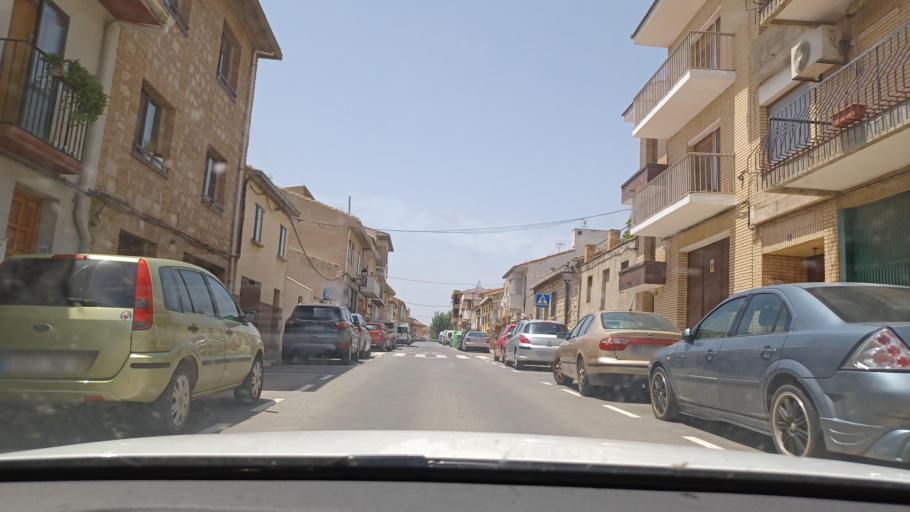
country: ES
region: Navarre
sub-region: Provincia de Navarra
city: Tudela
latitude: 42.0658
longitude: -1.6058
